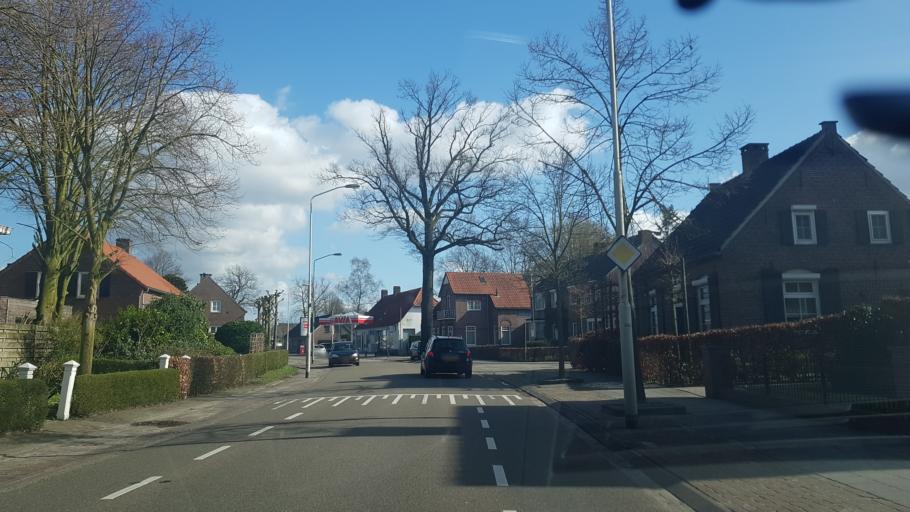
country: NL
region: North Brabant
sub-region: Gemeente Oirschot
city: Middelbeers
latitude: 51.4692
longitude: 5.2483
